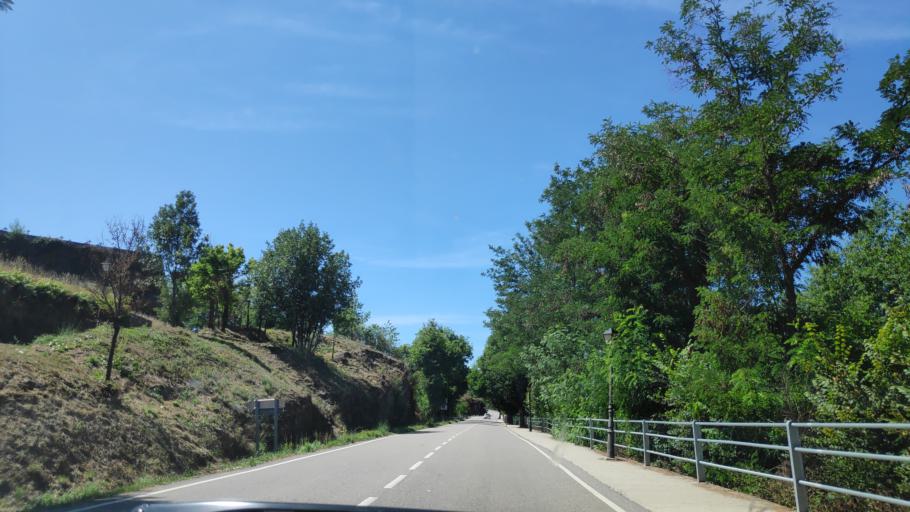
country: ES
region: Castille and Leon
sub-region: Provincia de Zamora
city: Puebla de Sanabria
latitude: 42.0573
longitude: -6.6348
